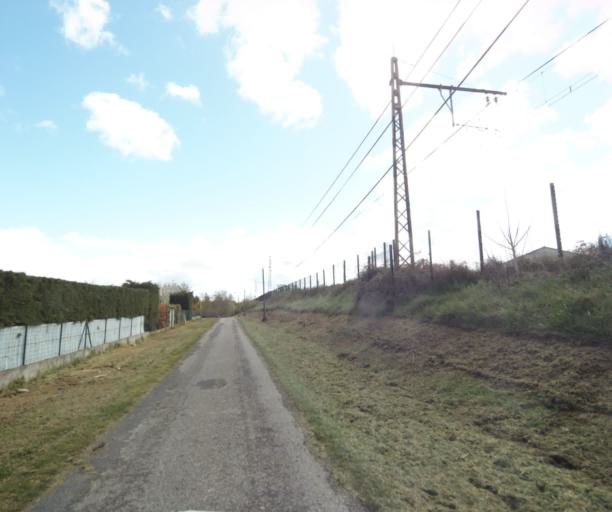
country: FR
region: Midi-Pyrenees
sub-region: Departement de l'Ariege
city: Saverdun
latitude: 43.2385
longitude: 1.5747
